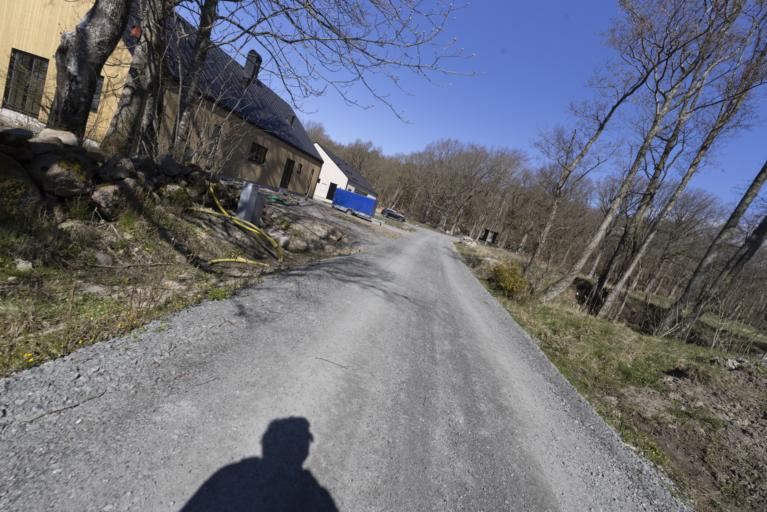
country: SE
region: Halland
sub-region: Varbergs Kommun
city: Varberg
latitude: 57.1616
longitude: 12.2604
